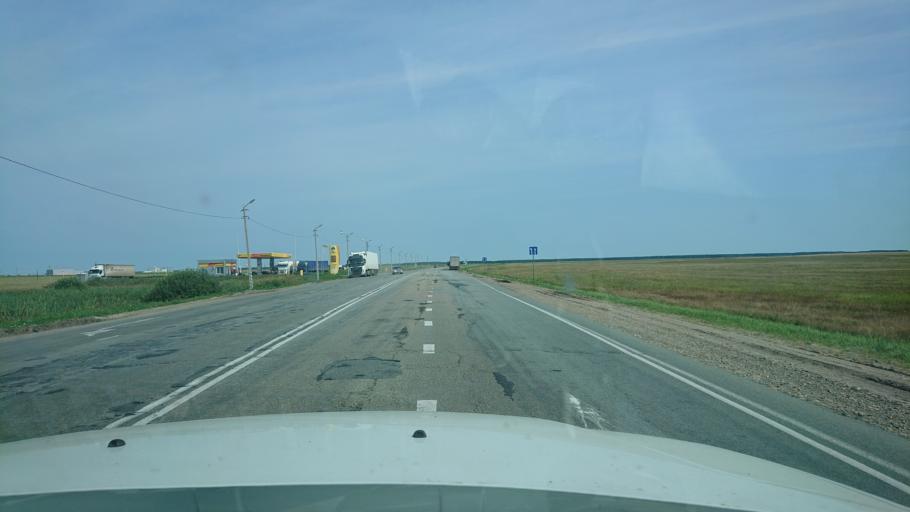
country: RU
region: Tjumen
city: Armizonskoye
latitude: 55.5352
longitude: 67.8926
